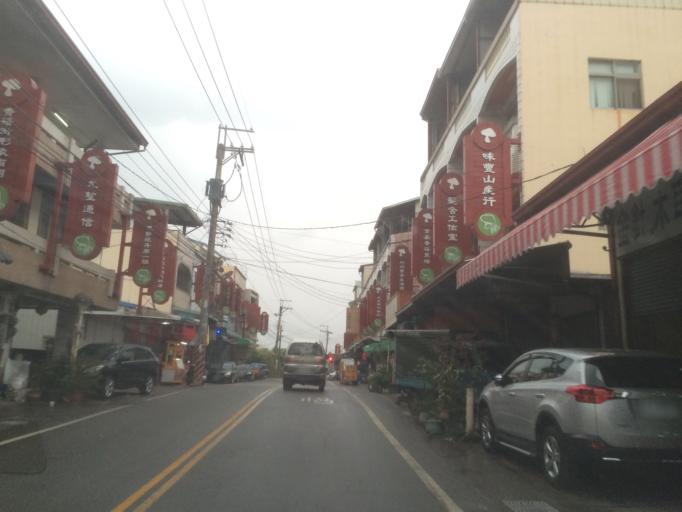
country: TW
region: Taiwan
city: Fengyuan
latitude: 24.1907
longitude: 120.8112
